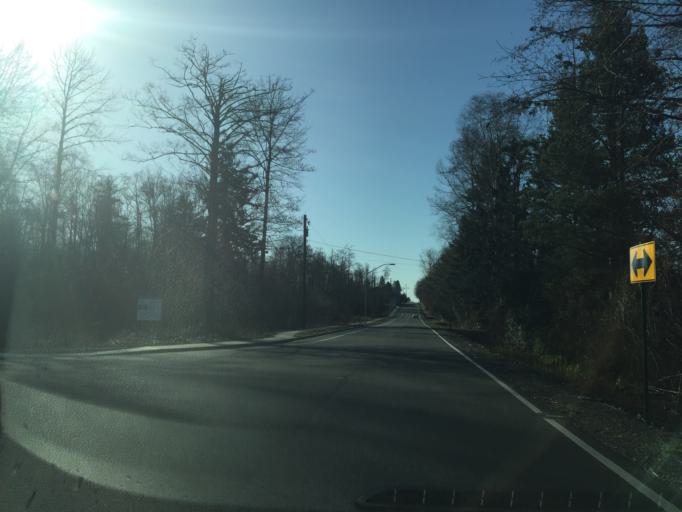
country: US
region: Washington
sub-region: Whatcom County
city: Bellingham
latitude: 48.7970
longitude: -122.5080
